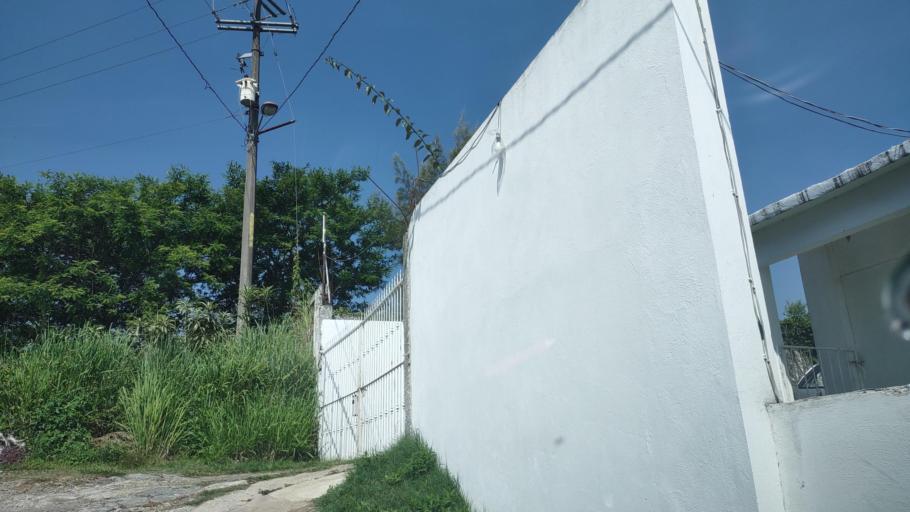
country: MX
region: Veracruz
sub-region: Emiliano Zapata
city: Dos Rios
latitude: 19.4940
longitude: -96.8188
